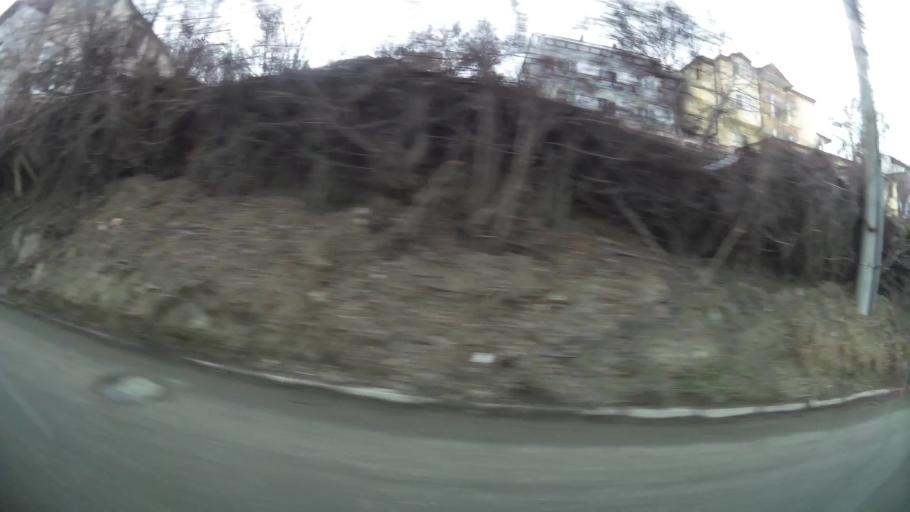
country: MK
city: Kondovo
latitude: 42.0111
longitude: 21.3174
